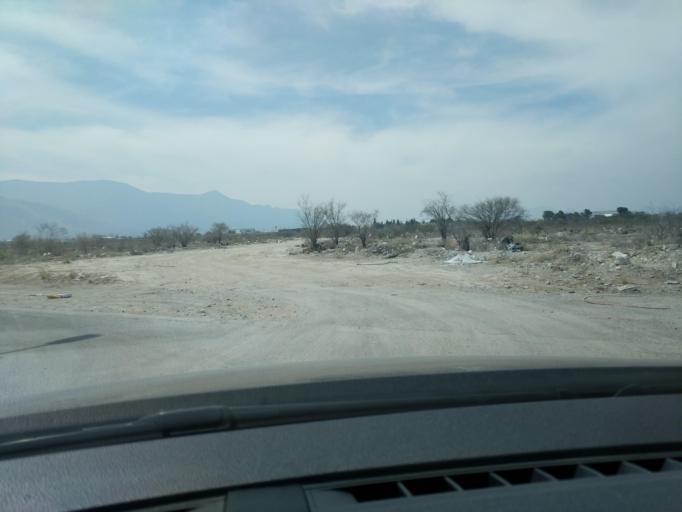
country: MX
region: Coahuila
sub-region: Arteaga
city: Arteaga
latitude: 25.4268
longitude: -100.9130
